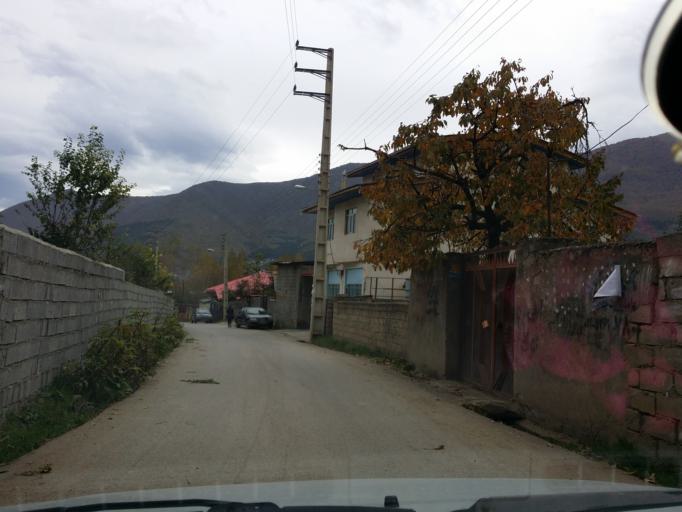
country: IR
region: Mazandaran
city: `Abbasabad
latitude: 36.5049
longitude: 51.1459
